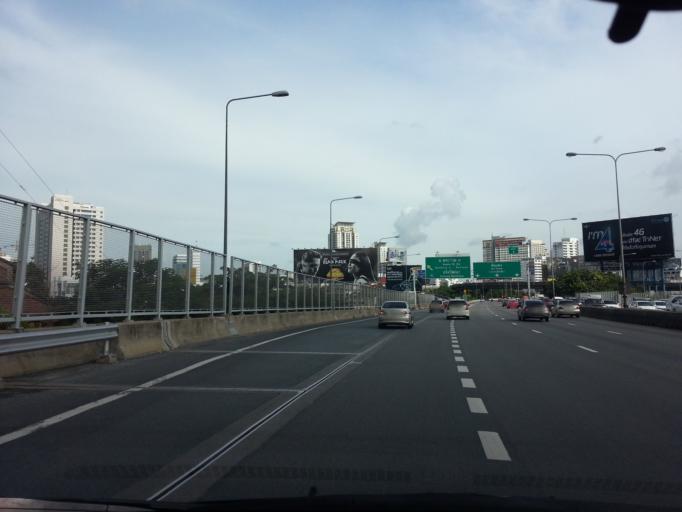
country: TH
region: Bangkok
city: Ratchathewi
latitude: 13.7546
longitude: 100.5458
